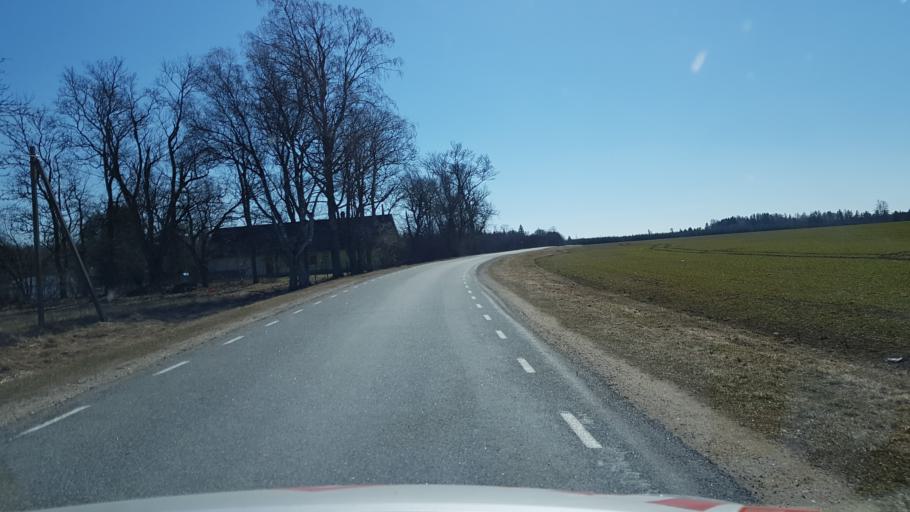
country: EE
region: Laeaene-Virumaa
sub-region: Rakke vald
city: Rakke
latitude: 59.0319
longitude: 26.3490
